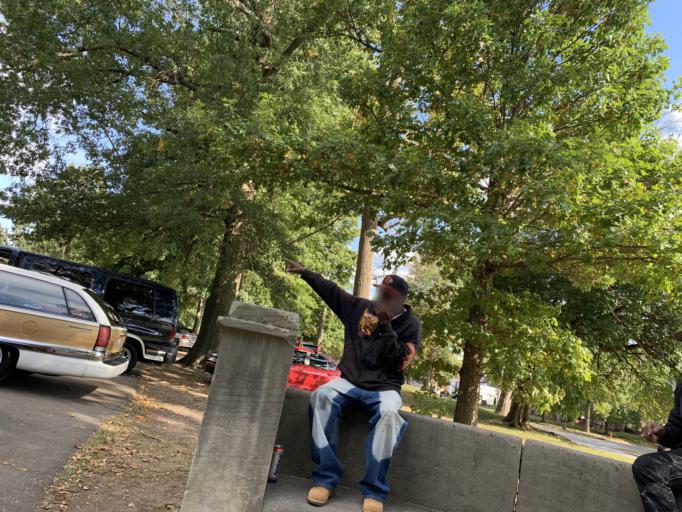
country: US
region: Indiana
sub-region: Floyd County
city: New Albany
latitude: 38.2510
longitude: -85.8299
